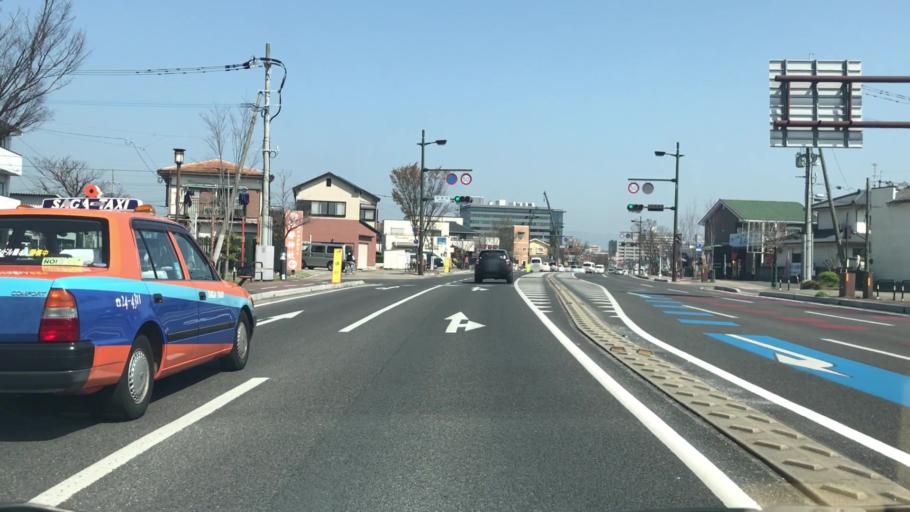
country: JP
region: Saga Prefecture
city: Saga-shi
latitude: 33.2524
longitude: 130.2921
